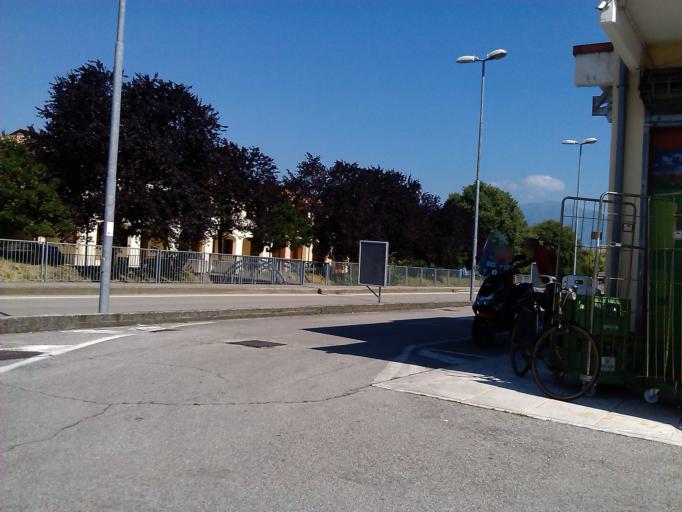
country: IT
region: Veneto
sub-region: Provincia di Treviso
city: Ca' Rainati
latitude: 45.7364
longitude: 11.8423
